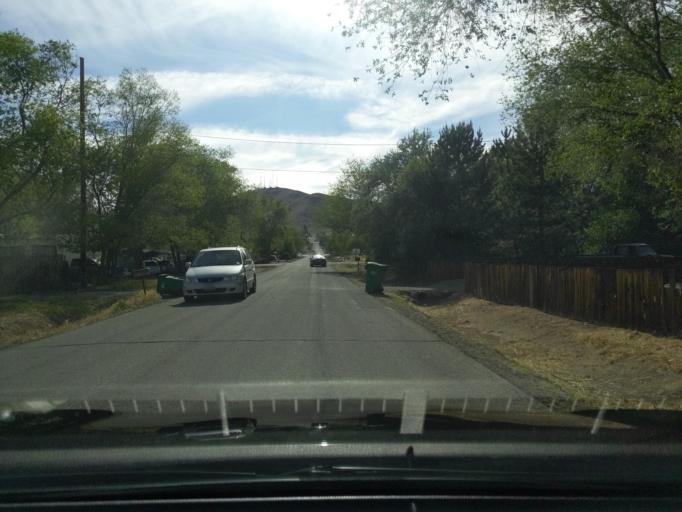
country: US
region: Nevada
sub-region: Washoe County
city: Sun Valley
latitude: 39.5855
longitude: -119.7770
